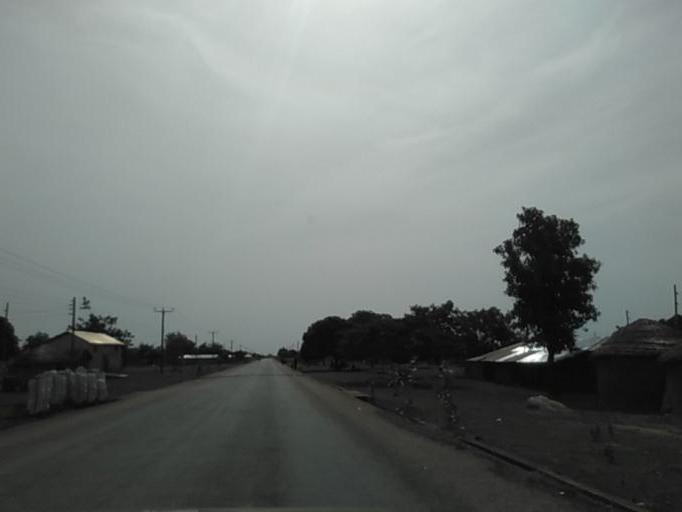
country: GH
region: Northern
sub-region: Yendi
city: Yendi
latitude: 9.4346
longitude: -0.1754
